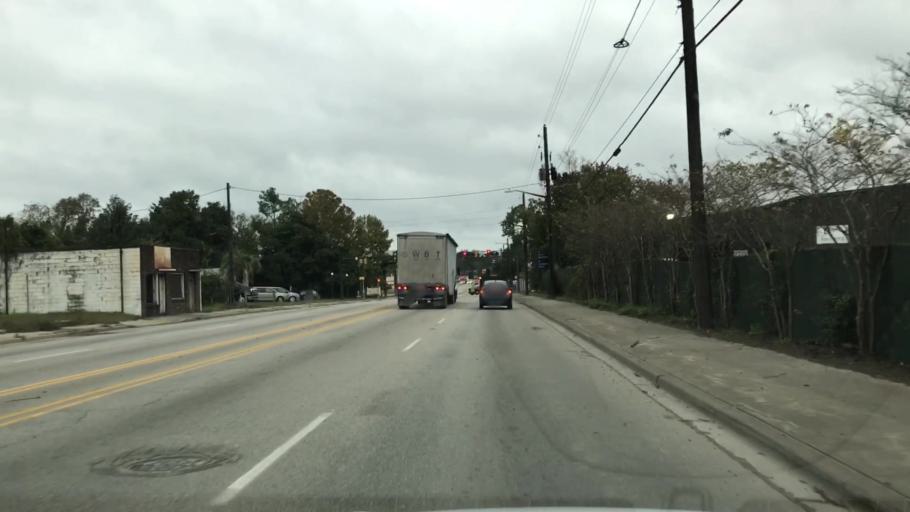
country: US
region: South Carolina
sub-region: Georgetown County
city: Georgetown
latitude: 33.3702
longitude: -79.2912
